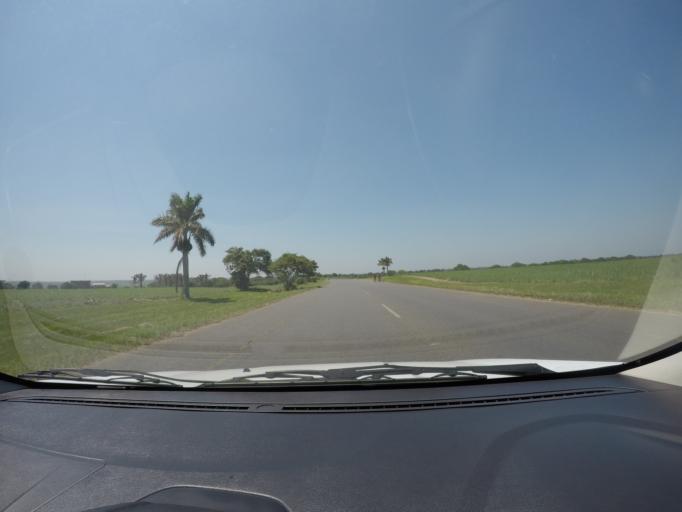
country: ZA
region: KwaZulu-Natal
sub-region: uThungulu District Municipality
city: Empangeni
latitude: -28.8036
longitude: 31.9581
